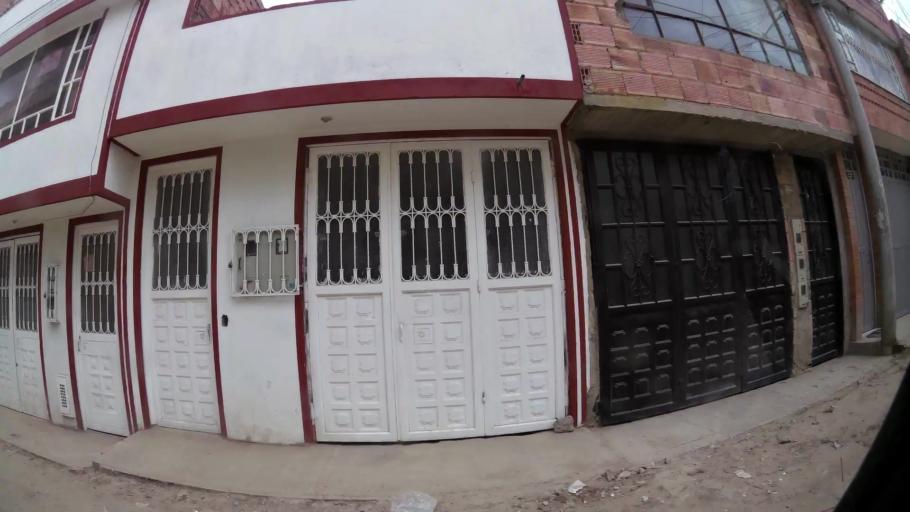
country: CO
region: Cundinamarca
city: Funza
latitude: 4.7206
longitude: -74.1338
